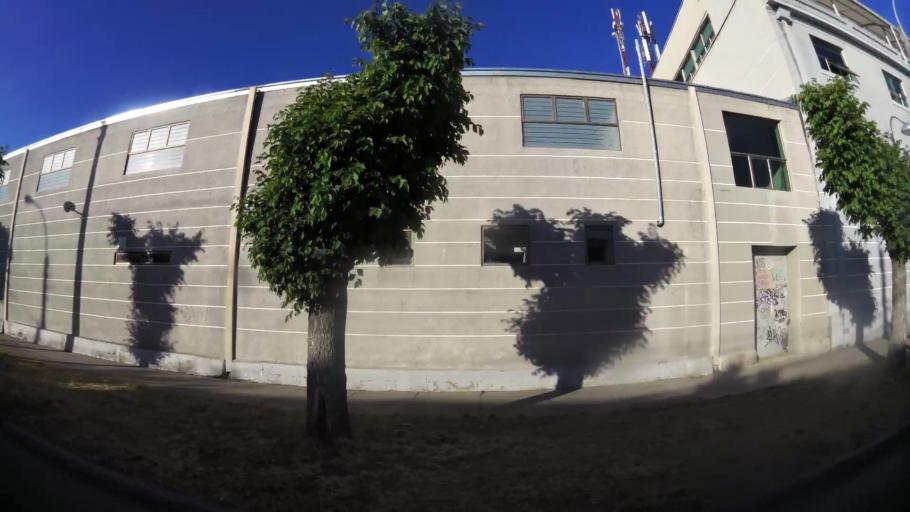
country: CL
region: Valparaiso
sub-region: Provincia de Valparaiso
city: Vina del Mar
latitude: -33.0272
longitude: -71.5404
